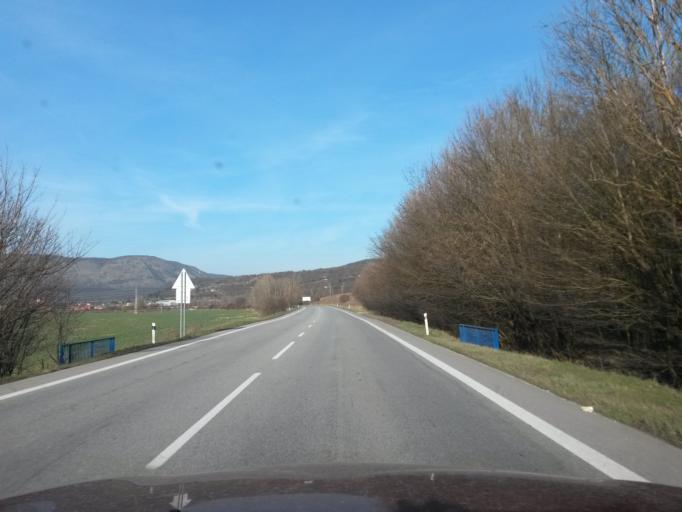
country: SK
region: Kosicky
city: Roznava
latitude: 48.5300
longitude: 20.3917
